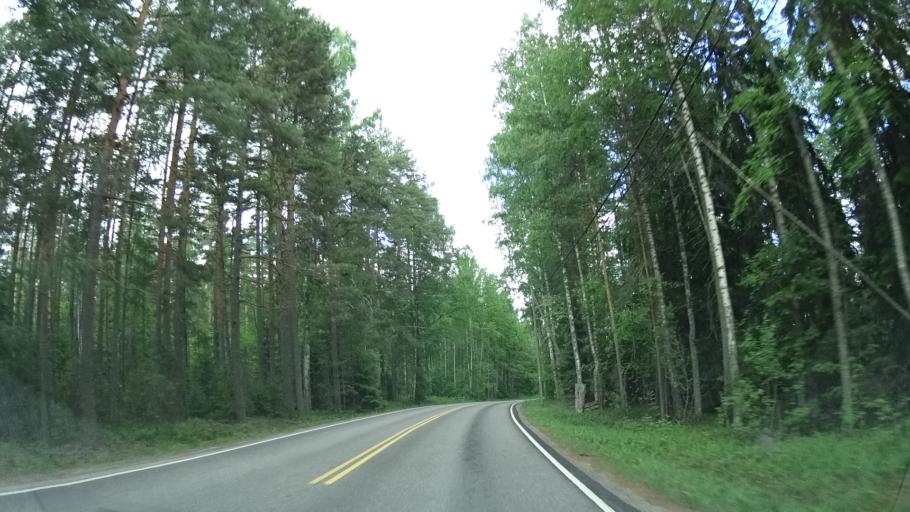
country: FI
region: Paijanne Tavastia
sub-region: Lahti
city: Asikkala
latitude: 61.3216
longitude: 25.5568
